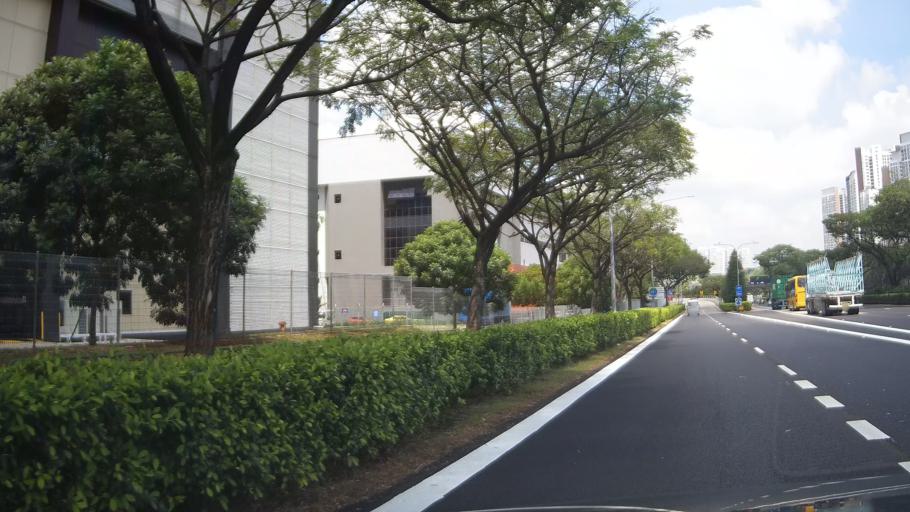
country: SG
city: Singapore
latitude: 1.3400
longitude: 103.7512
